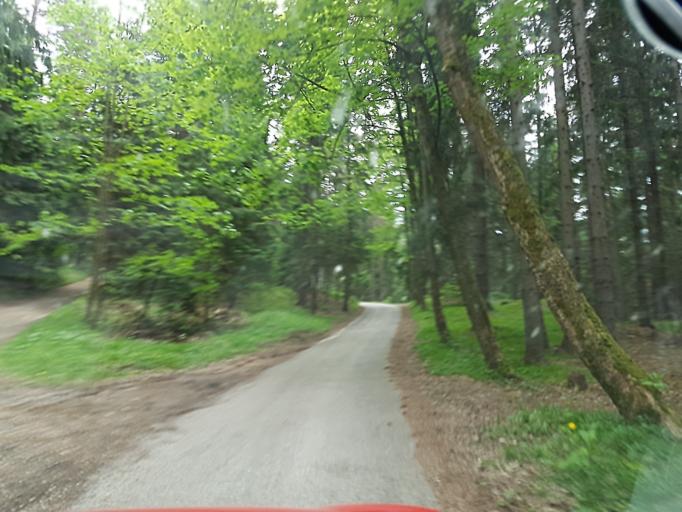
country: SK
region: Zilinsky
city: Ruzomberok
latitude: 49.0658
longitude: 19.2744
